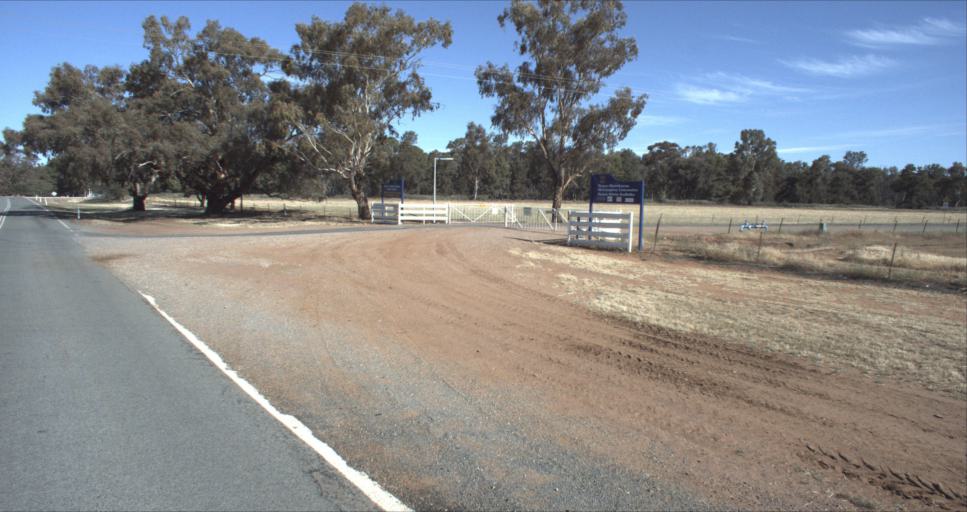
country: AU
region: New South Wales
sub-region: Leeton
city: Leeton
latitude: -34.6250
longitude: 146.3897
